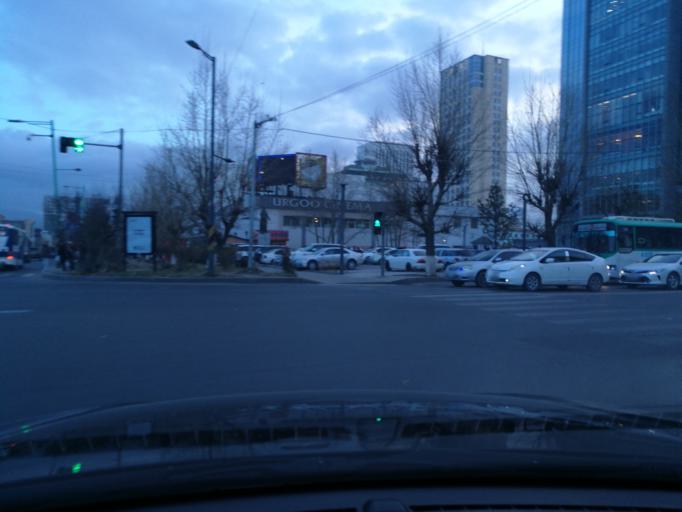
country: MN
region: Ulaanbaatar
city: Ulaanbaatar
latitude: 47.9228
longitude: 106.9228
